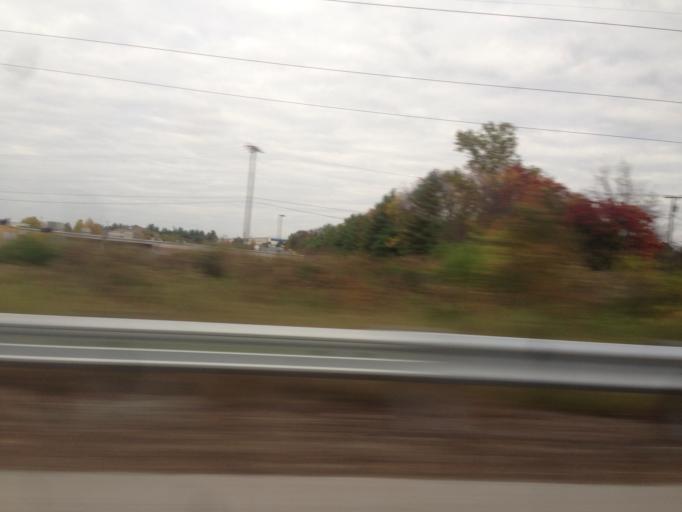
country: US
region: Tennessee
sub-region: Davidson County
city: Lakewood
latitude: 36.1423
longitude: -86.6746
